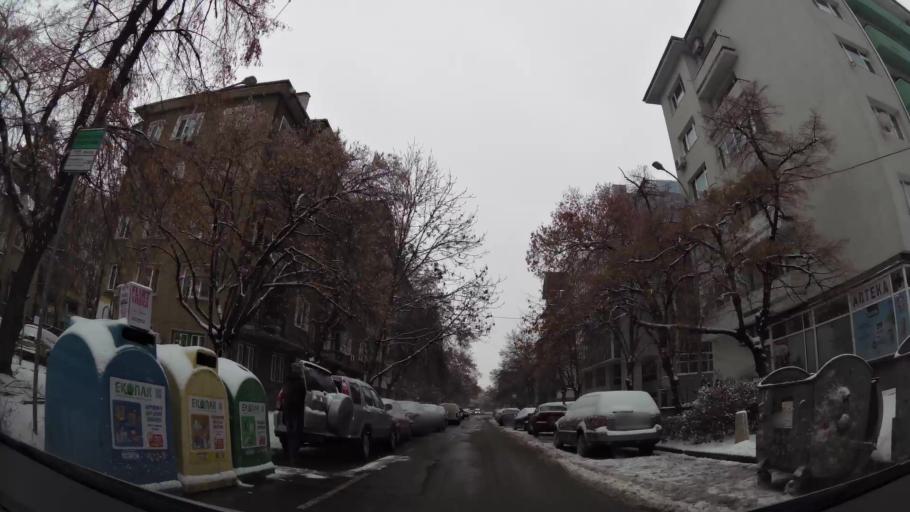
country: BG
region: Sofia-Capital
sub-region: Stolichna Obshtina
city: Sofia
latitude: 42.6949
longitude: 23.3111
